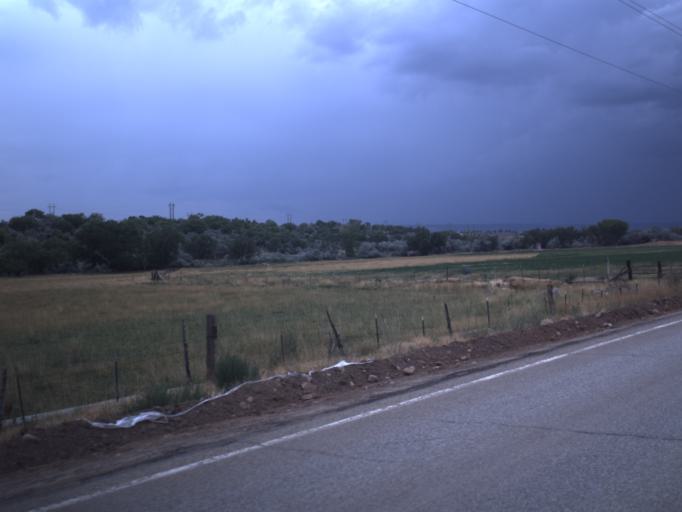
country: US
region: Utah
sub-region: Duchesne County
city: Roosevelt
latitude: 40.3234
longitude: -110.0167
